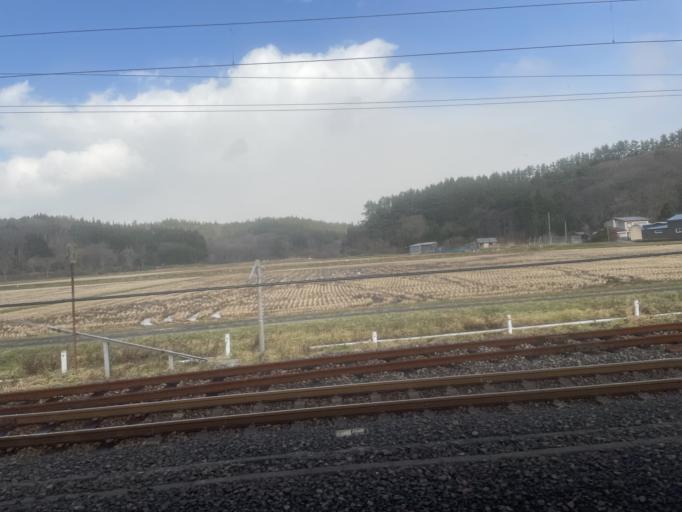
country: JP
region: Aomori
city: Aomori Shi
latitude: 41.0617
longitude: 140.5790
